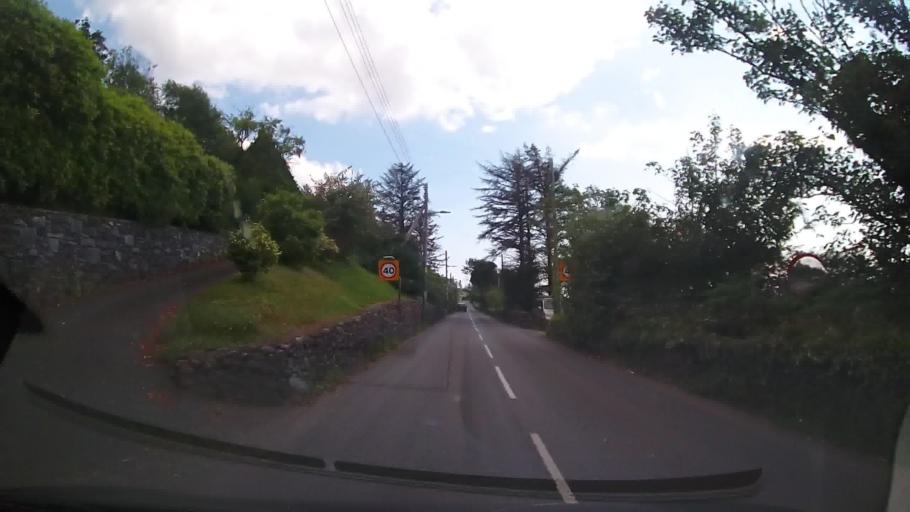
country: GB
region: Wales
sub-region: Gwynedd
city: Llanfair
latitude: 52.8509
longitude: -4.1134
